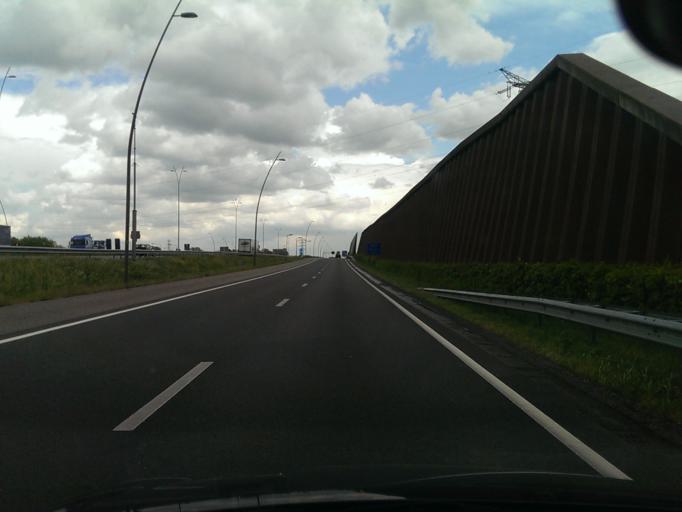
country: NL
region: North Brabant
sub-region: Gemeente Waalre
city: Waalre
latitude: 51.4053
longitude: 5.4585
